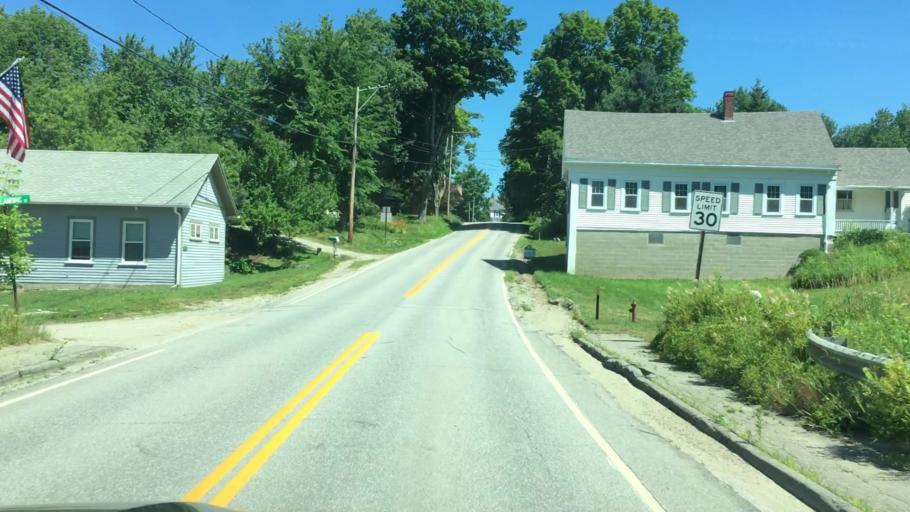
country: US
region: Maine
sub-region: Hancock County
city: Penobscot
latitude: 44.4527
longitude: -68.7027
